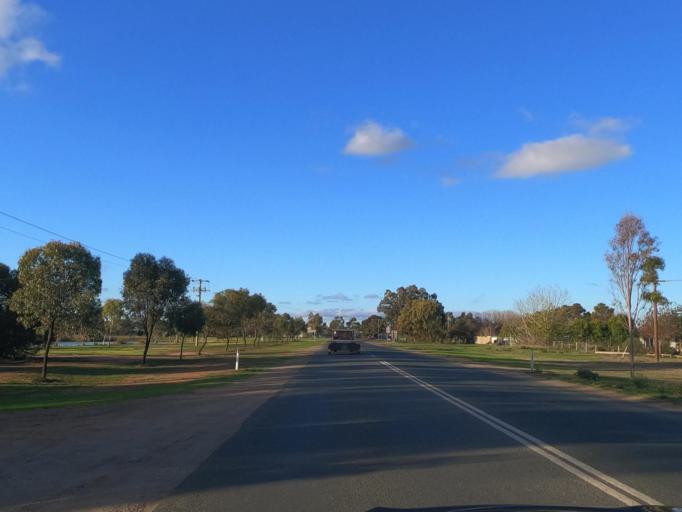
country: AU
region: Victoria
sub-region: Swan Hill
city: Swan Hill
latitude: -35.3408
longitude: 143.5375
